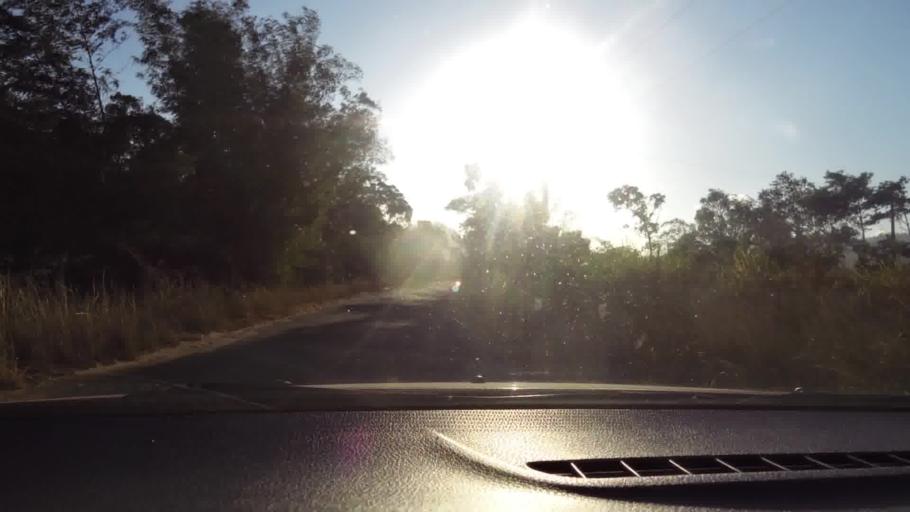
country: BR
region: Espirito Santo
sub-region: Guarapari
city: Guarapari
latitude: -20.5301
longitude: -40.4689
